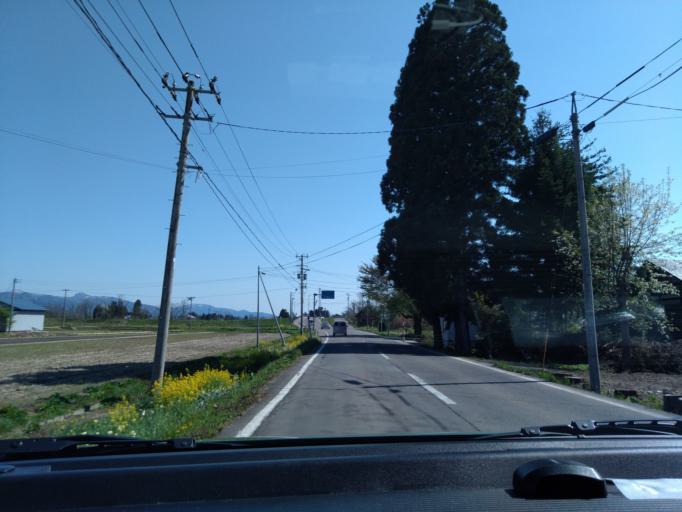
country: JP
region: Akita
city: Kakunodatemachi
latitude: 39.5465
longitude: 140.5857
